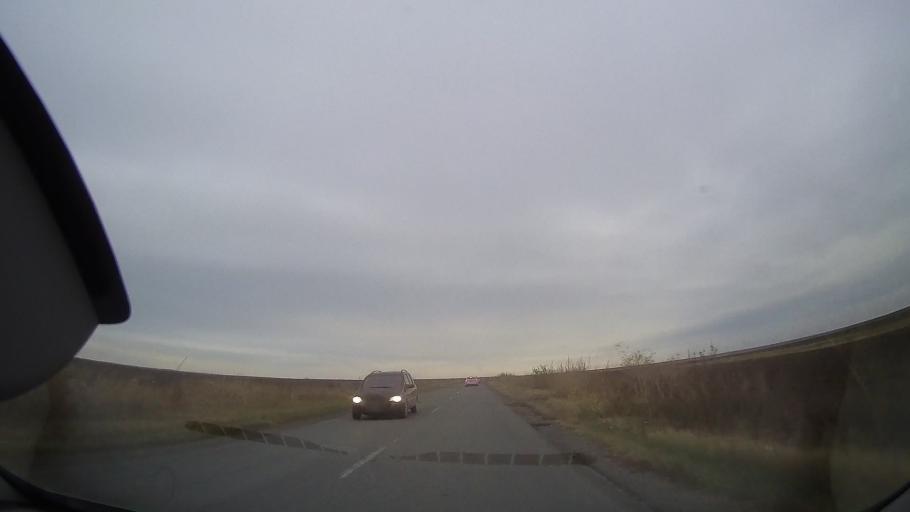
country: RO
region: Ialomita
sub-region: Oras Amara
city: Amara
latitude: 44.6636
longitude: 27.3007
